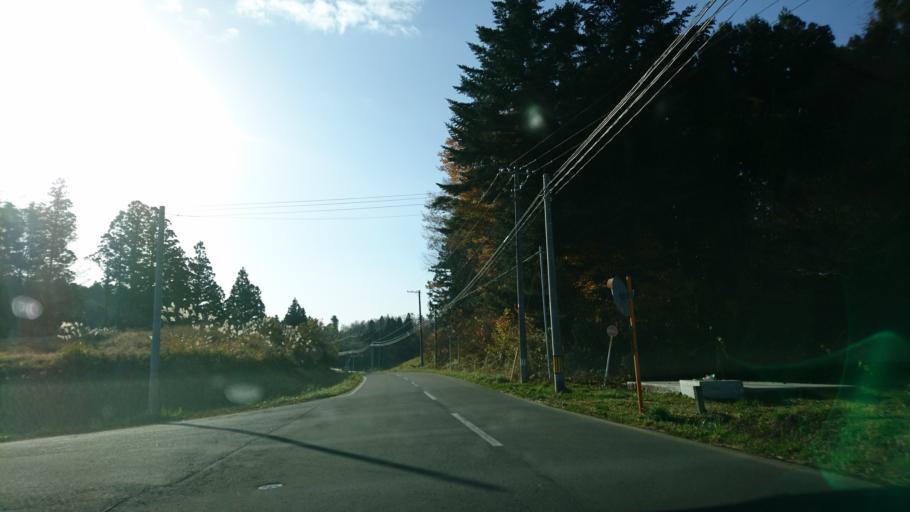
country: JP
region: Iwate
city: Ichinoseki
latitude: 38.8784
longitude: 141.2915
